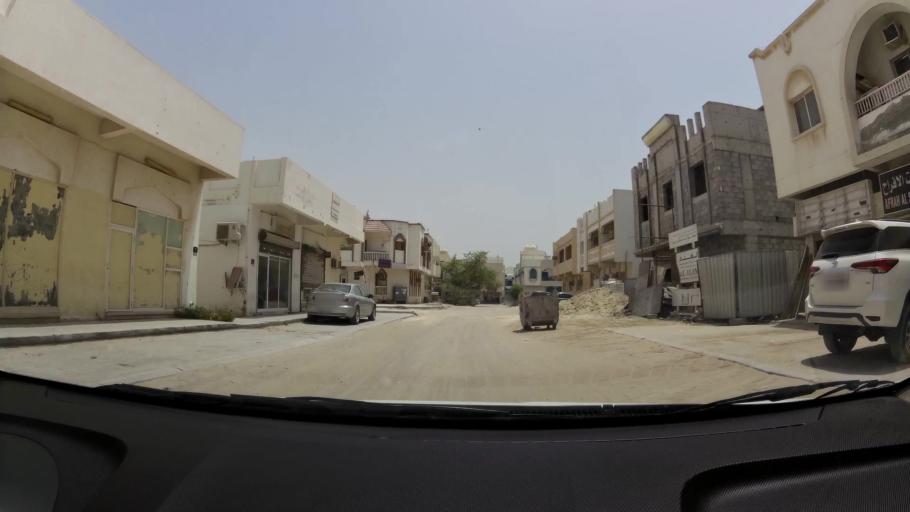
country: AE
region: Ash Shariqah
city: Sharjah
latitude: 25.3541
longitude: 55.4060
